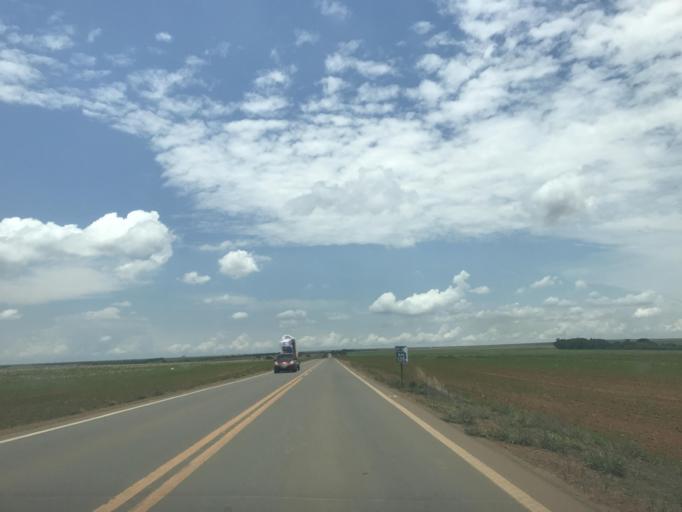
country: BR
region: Goias
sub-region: Luziania
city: Luziania
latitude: -16.4979
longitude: -48.2039
